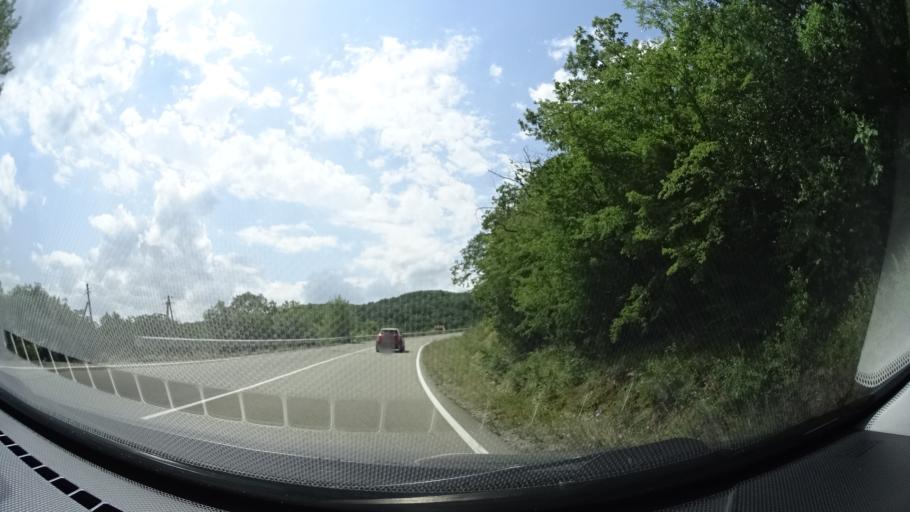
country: GE
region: Kakheti
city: Sagarejo
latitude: 41.7811
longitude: 45.1539
